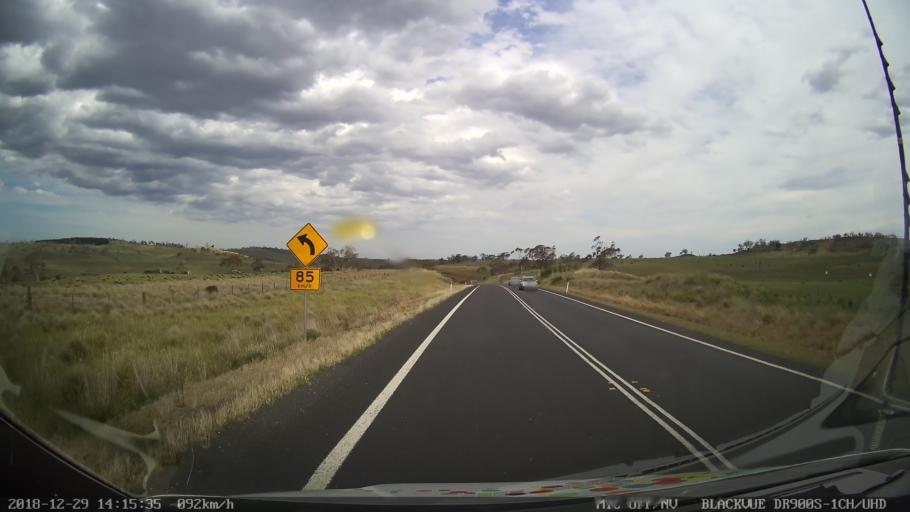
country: AU
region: New South Wales
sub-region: Cooma-Monaro
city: Cooma
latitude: -36.4576
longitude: 149.2422
